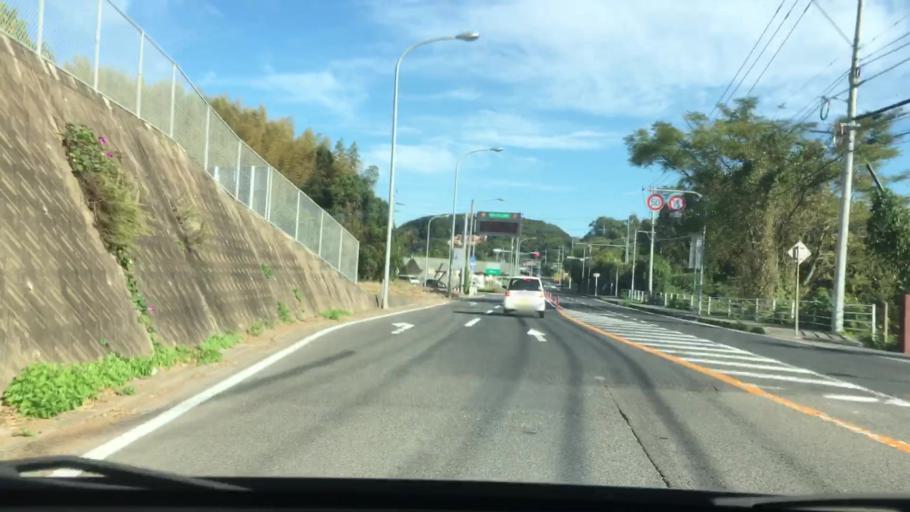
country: JP
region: Nagasaki
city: Sasebo
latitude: 33.0632
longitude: 129.7643
